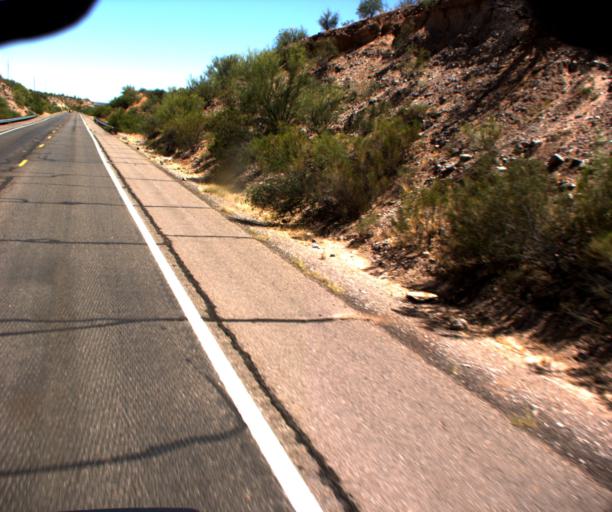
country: US
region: Arizona
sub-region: Pinal County
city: Mammoth
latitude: 32.7579
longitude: -110.6503
